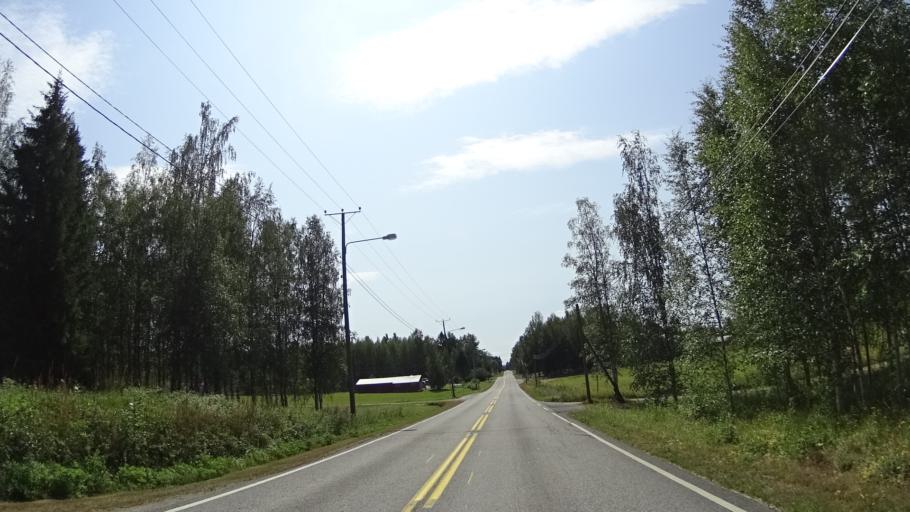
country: FI
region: Pirkanmaa
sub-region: Ylae-Pirkanmaa
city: Maenttae
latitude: 61.8946
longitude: 24.7934
